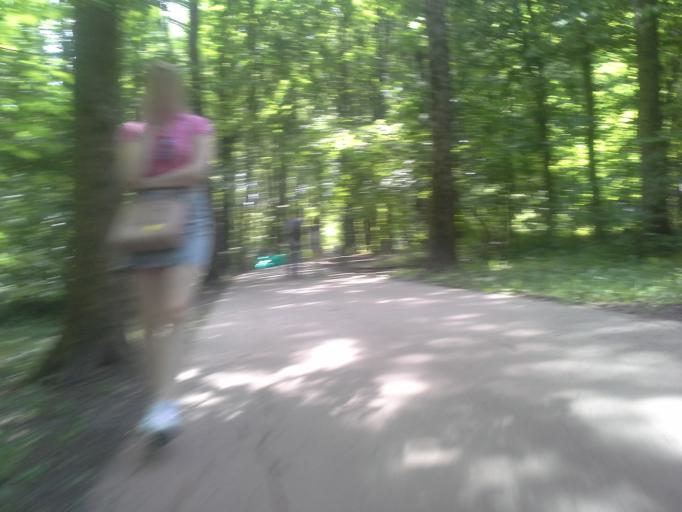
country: RU
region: Moscow
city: Chertanovo Yuzhnoye
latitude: 55.5936
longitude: 37.5860
